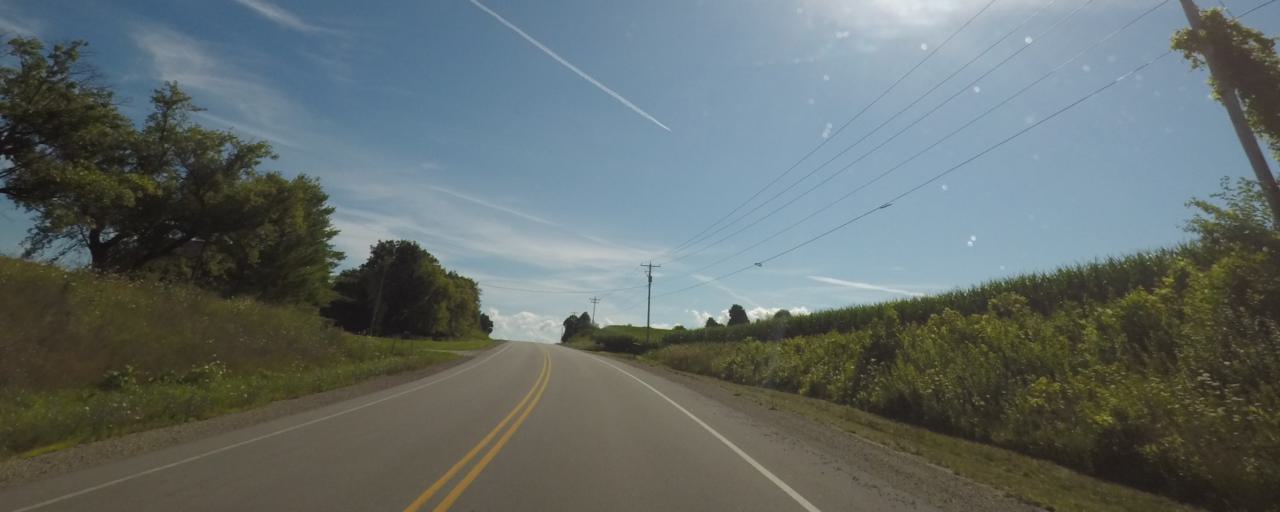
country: US
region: Wisconsin
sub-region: Jefferson County
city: Johnson Creek
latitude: 43.0713
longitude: -88.6913
